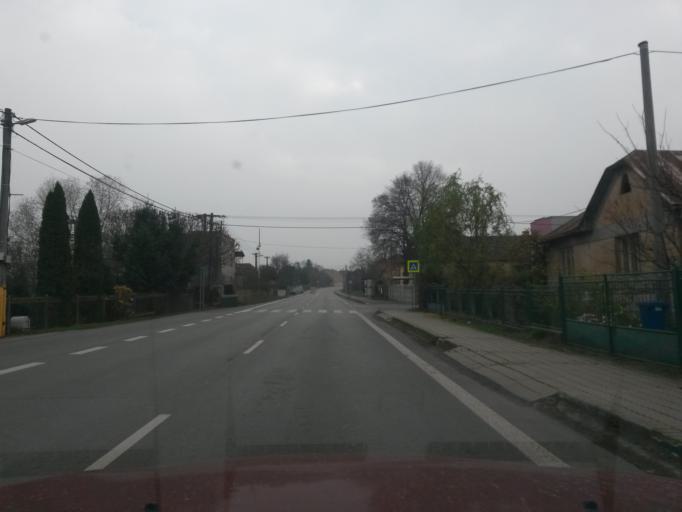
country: SK
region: Kosicky
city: Kosice
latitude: 48.8287
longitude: 21.2955
